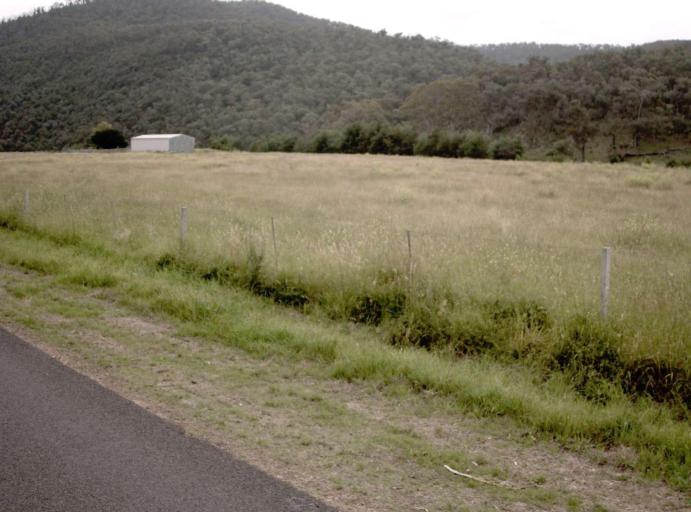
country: AU
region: Victoria
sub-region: Wellington
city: Heyfield
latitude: -37.7968
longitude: 146.6751
